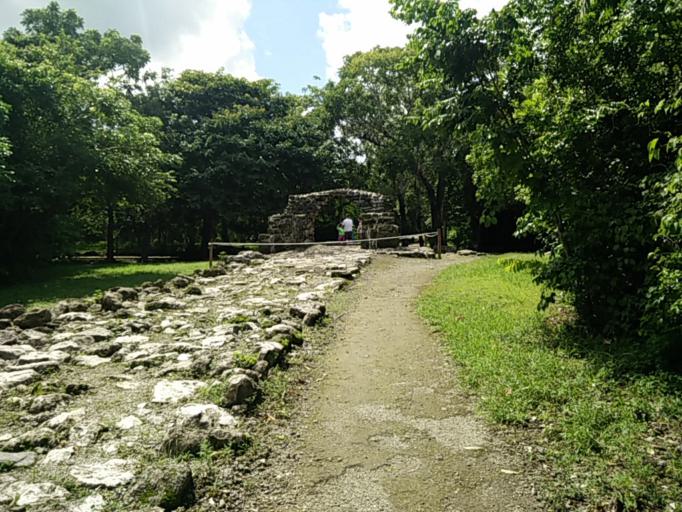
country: MX
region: Quintana Roo
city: San Miguel de Cozumel
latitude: 20.5007
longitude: -86.8453
